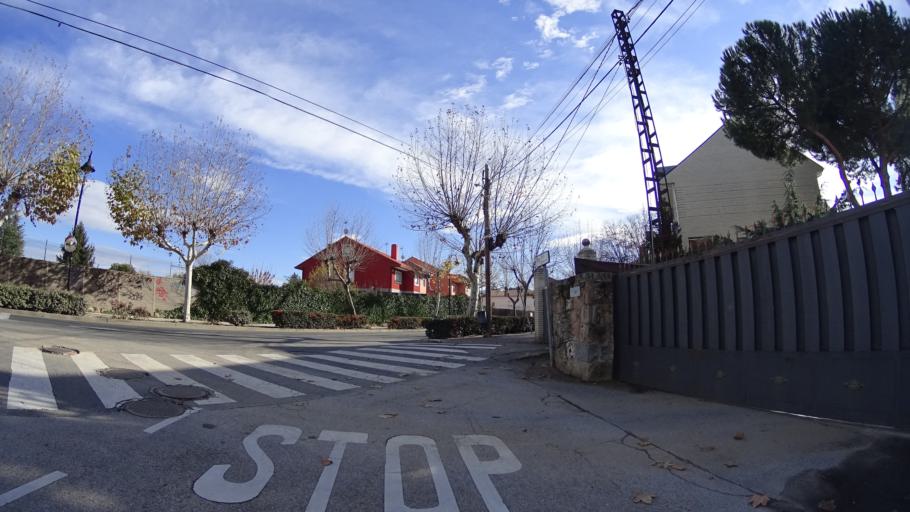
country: ES
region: Madrid
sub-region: Provincia de Madrid
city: Galapagar
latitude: 40.5774
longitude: -4.0104
